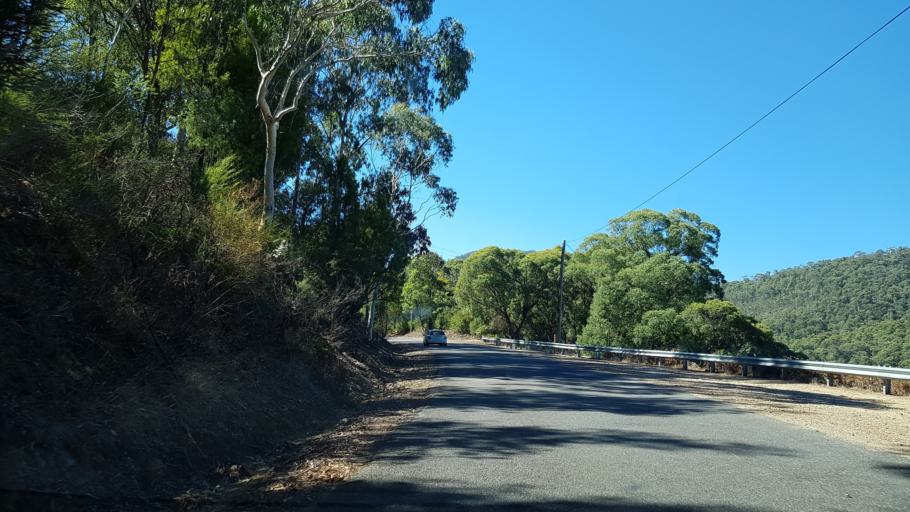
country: AU
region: Victoria
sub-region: Mansfield
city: Mansfield
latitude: -36.9121
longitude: 146.3892
